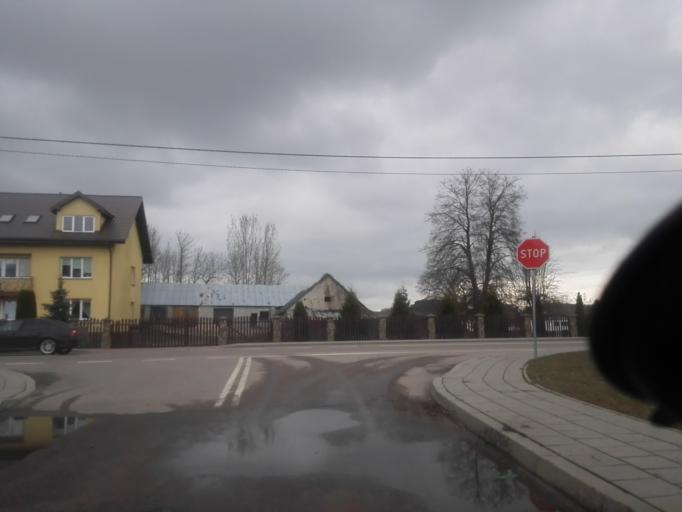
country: PL
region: Podlasie
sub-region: Suwalki
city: Suwalki
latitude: 54.2069
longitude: 22.9130
